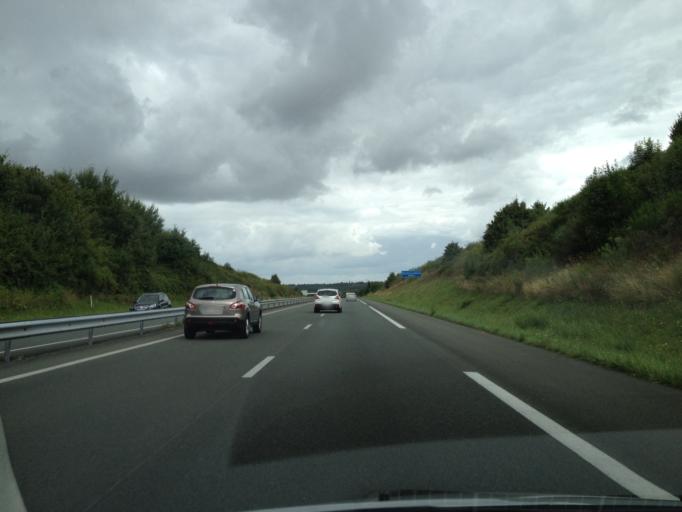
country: FR
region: Pays de la Loire
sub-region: Departement de la Vendee
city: Saint-Martin-des-Noyers
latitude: 46.7468
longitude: -1.1634
